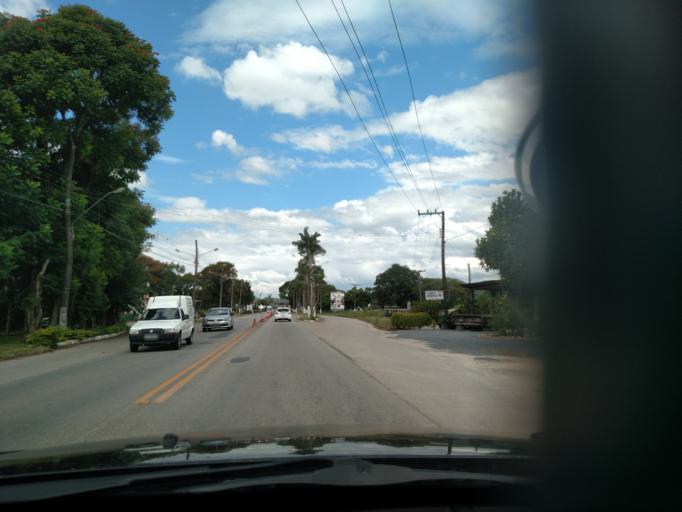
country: BR
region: Santa Catarina
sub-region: Gaspar
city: Gaspar
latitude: -26.9190
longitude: -48.9029
